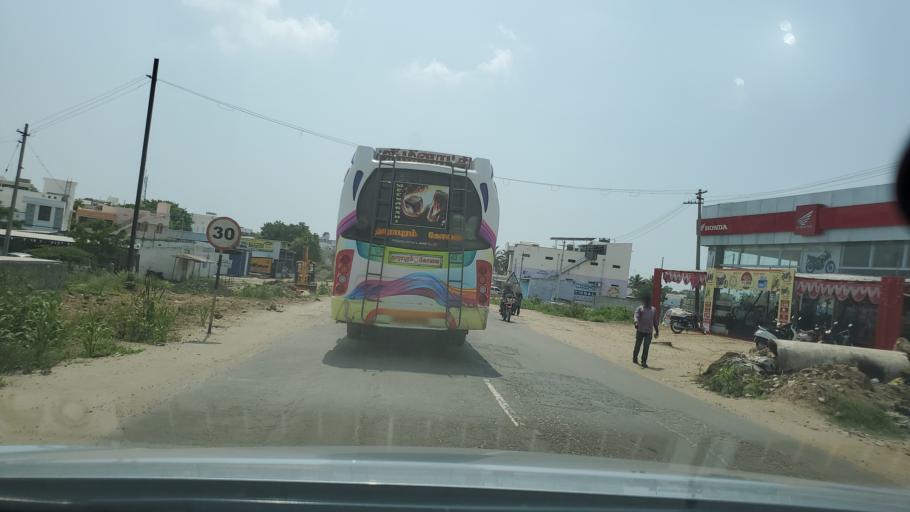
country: IN
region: Tamil Nadu
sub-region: Tiruppur
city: Dharapuram
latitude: 10.7381
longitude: 77.5176
